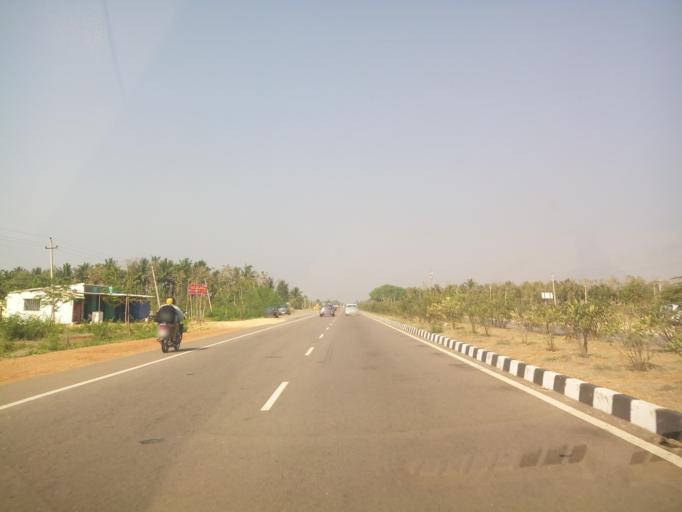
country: IN
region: Karnataka
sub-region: Tumkur
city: Kunigal
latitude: 12.9950
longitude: 76.9008
